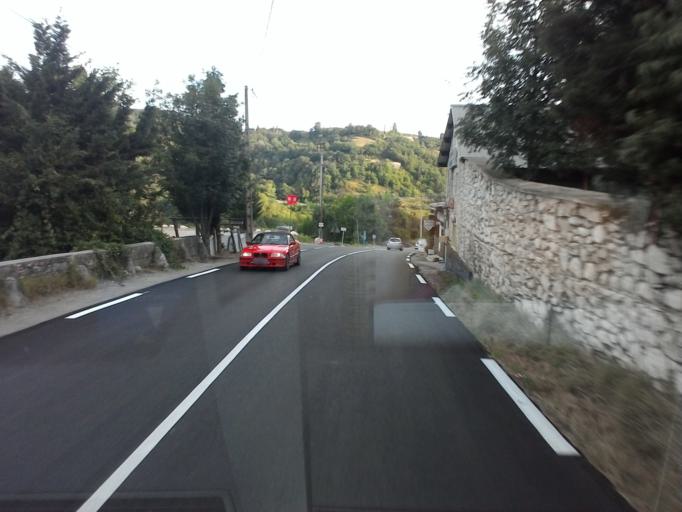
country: FR
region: Rhone-Alpes
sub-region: Departement de l'Isere
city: La Mure
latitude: 44.8957
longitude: 5.8174
